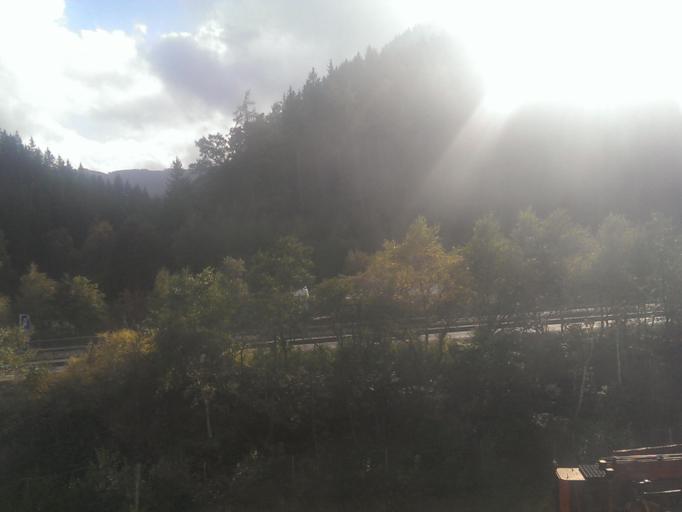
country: AT
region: Styria
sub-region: Politischer Bezirk Leoben
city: Kammern im Liesingtal
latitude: 47.3880
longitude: 14.8879
